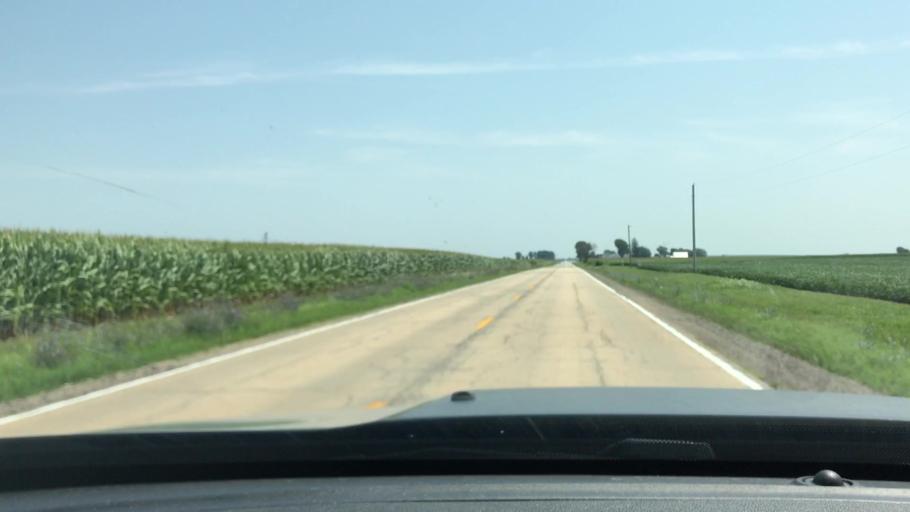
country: US
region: Illinois
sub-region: LaSalle County
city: Ottawa
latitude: 41.4703
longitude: -88.8540
